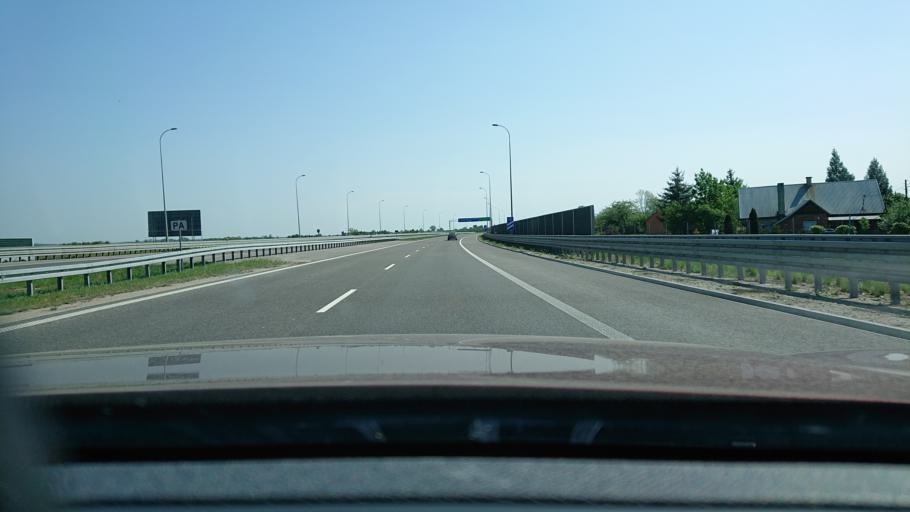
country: PL
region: Subcarpathian Voivodeship
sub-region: Powiat lancucki
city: Lancut
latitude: 50.0979
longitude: 22.2130
